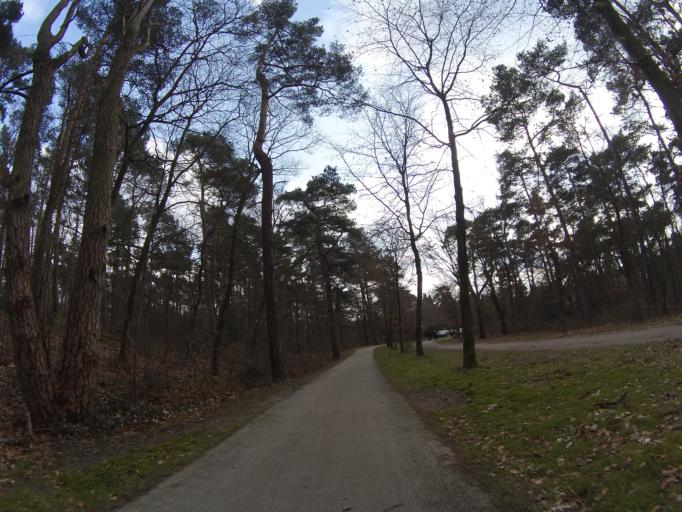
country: NL
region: Utrecht
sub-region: Gemeente Soest
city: Soest
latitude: 52.1482
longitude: 5.2993
